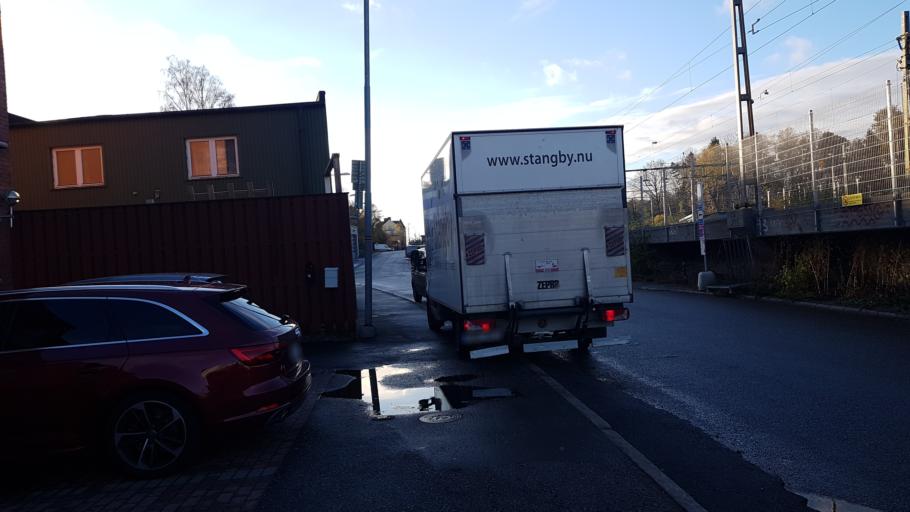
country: SE
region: Stockholm
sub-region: Solna Kommun
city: Solna
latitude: 59.3591
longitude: 18.0124
